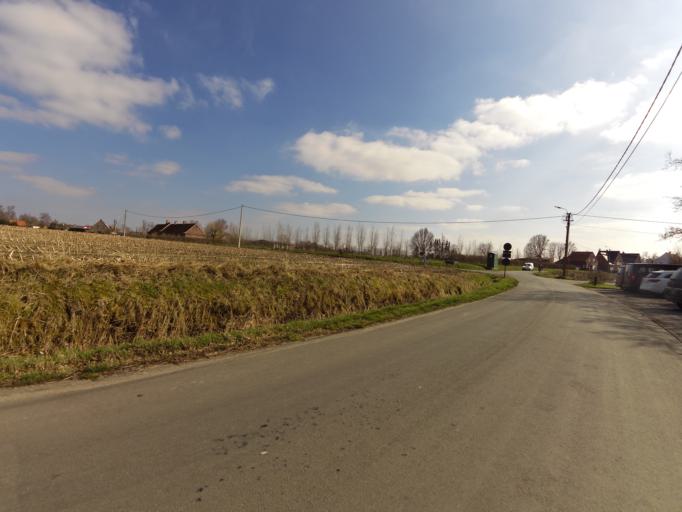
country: BE
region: Flanders
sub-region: Provincie West-Vlaanderen
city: Torhout
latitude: 51.0533
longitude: 3.0960
